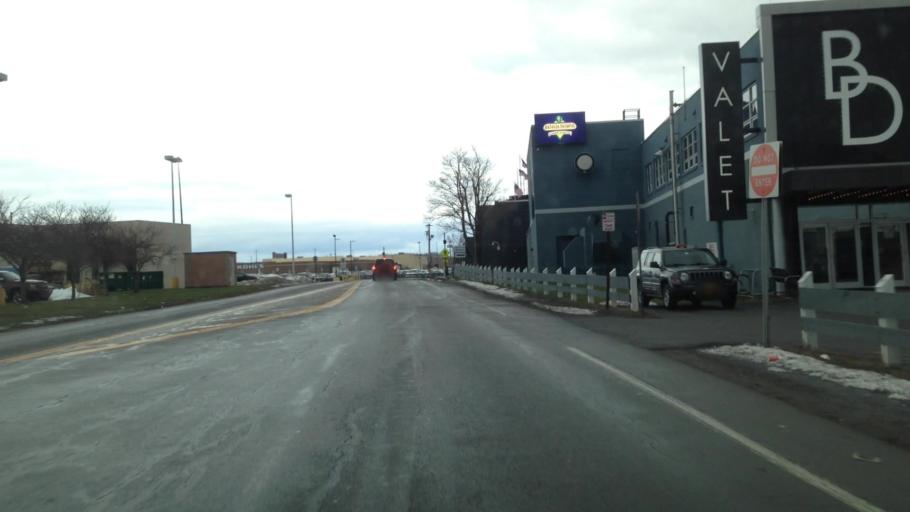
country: US
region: New York
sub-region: Genesee County
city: Batavia
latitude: 43.0088
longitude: -78.2060
